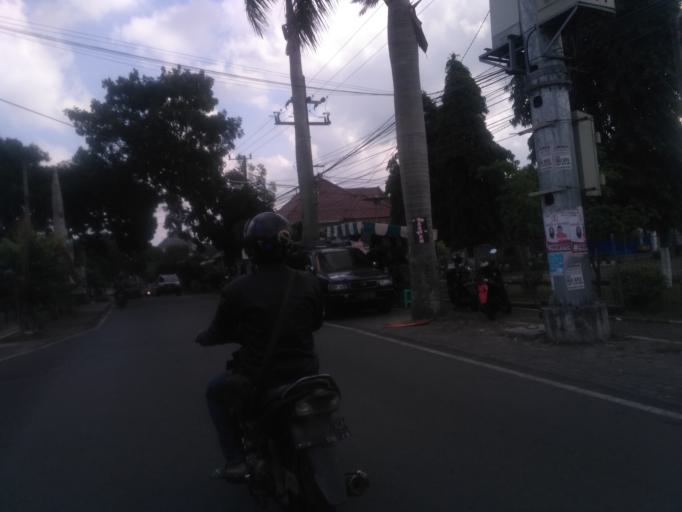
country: ID
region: East Java
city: Malang
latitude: -7.9428
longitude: 112.6316
